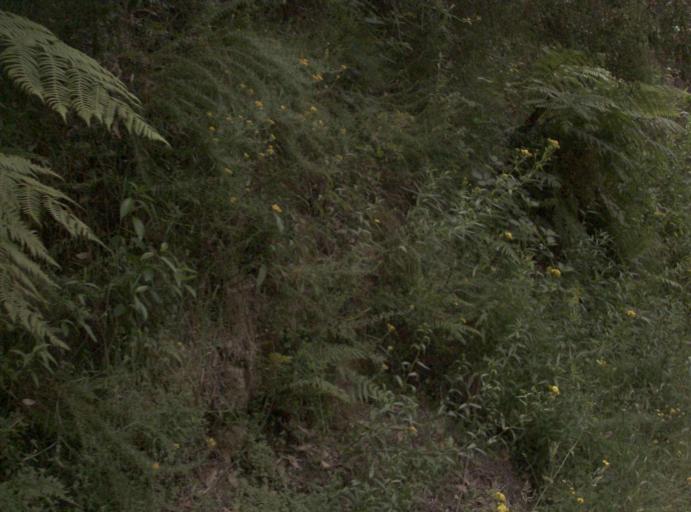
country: AU
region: Victoria
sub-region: Latrobe
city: Moe
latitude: -37.8165
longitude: 146.1705
